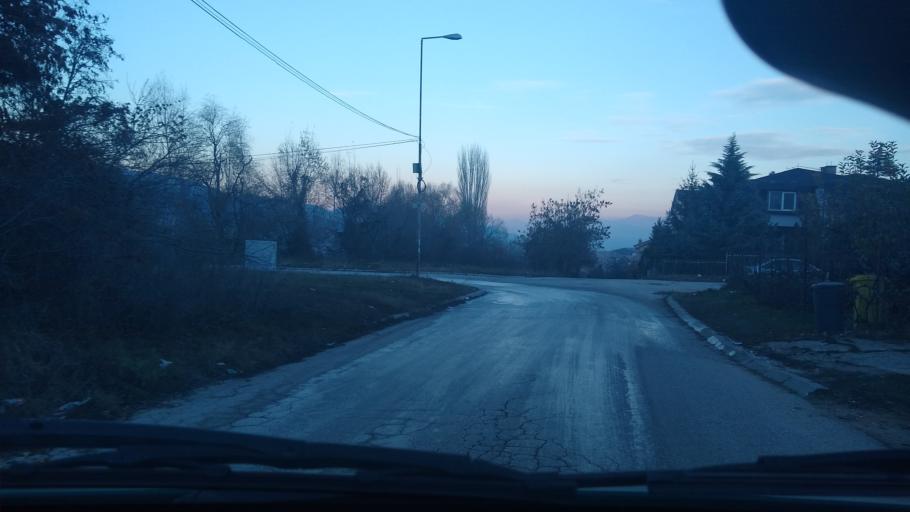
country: MK
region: Bitola
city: Bitola
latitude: 41.0259
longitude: 21.3037
